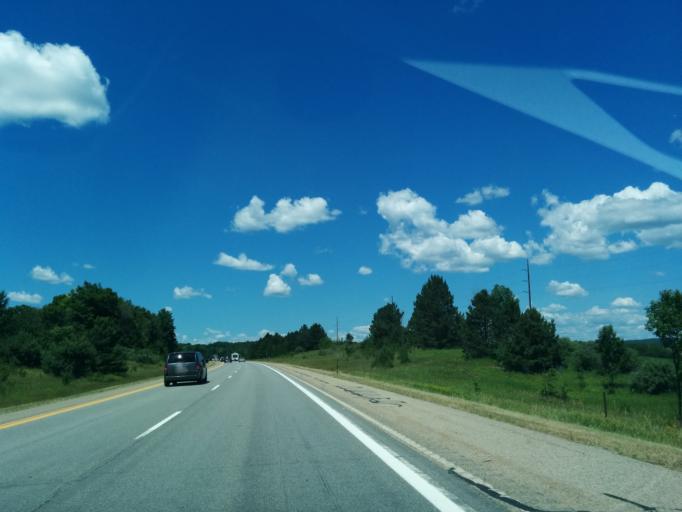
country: US
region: Michigan
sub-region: Ogemaw County
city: West Branch
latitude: 44.2571
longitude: -84.2487
